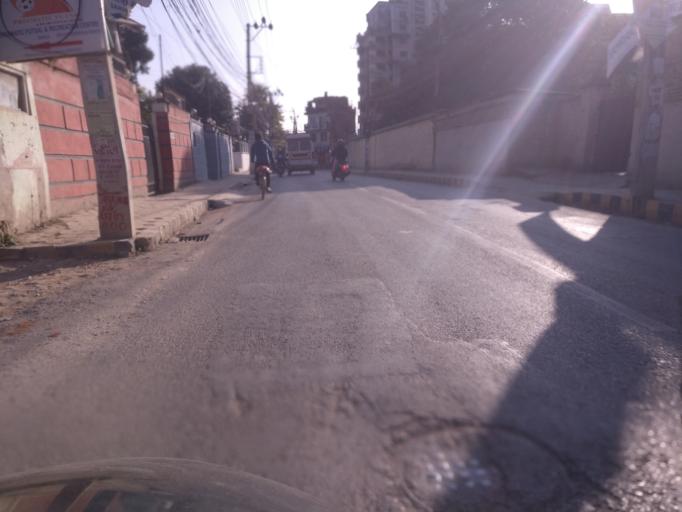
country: NP
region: Central Region
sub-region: Bagmati Zone
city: Patan
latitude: 27.6811
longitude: 85.3057
